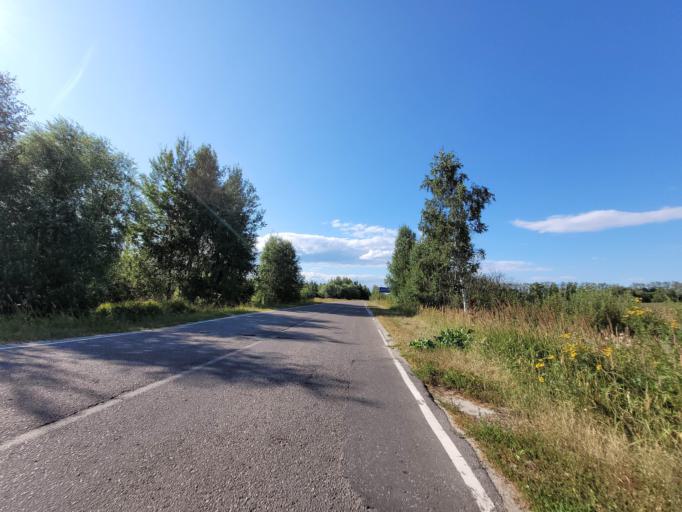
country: RU
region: Moskovskaya
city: Konobeyevo
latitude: 55.4012
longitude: 38.7096
